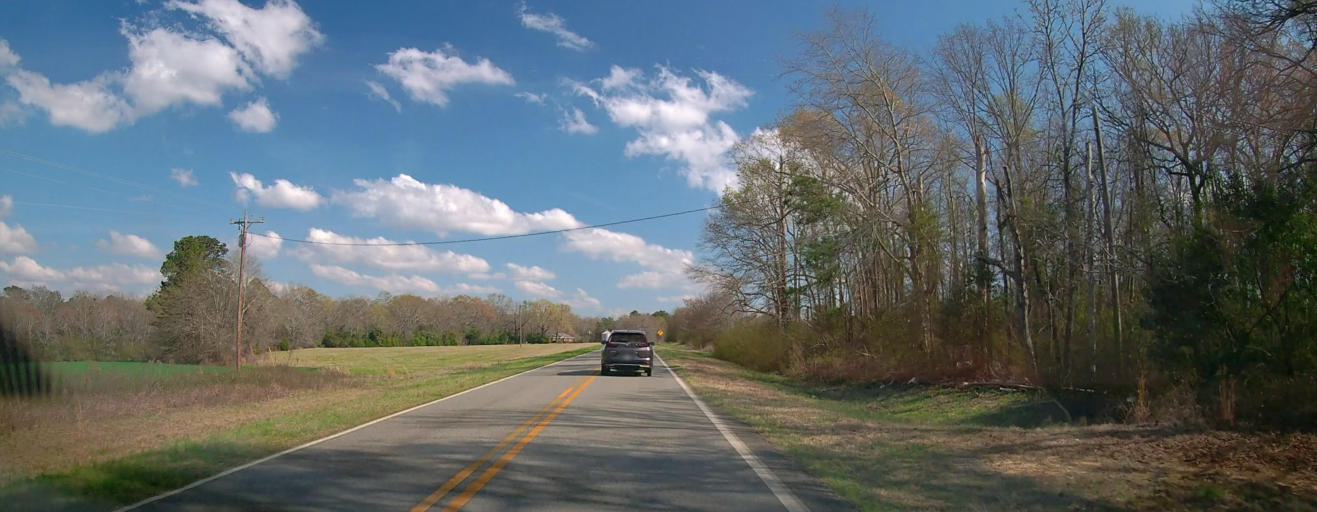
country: US
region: Georgia
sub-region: Wilkinson County
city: Irwinton
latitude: 32.6284
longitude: -83.0968
